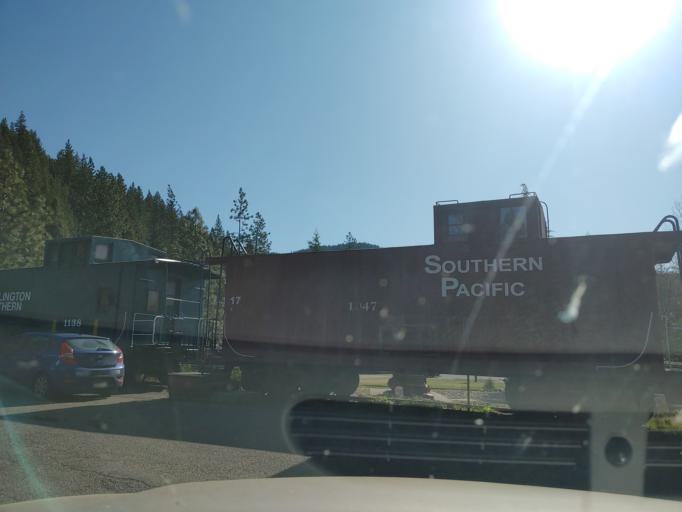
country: US
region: California
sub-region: Siskiyou County
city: Dunsmuir
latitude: 41.1848
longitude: -122.2932
